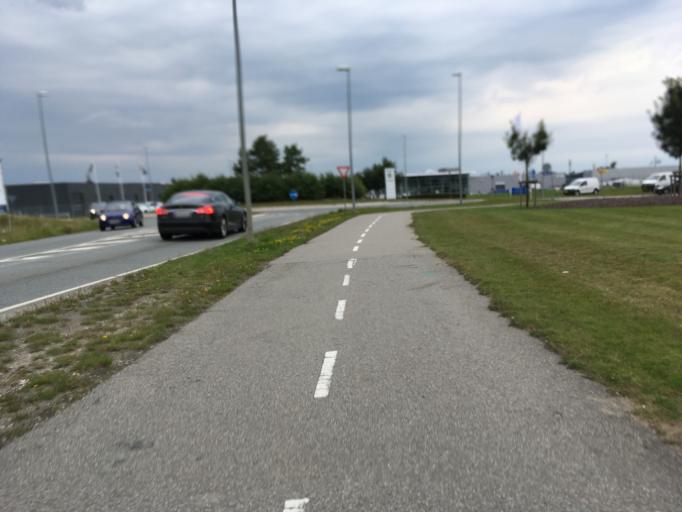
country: DK
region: Capital Region
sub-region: Hillerod Kommune
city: Hillerod
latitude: 55.9270
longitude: 12.2632
